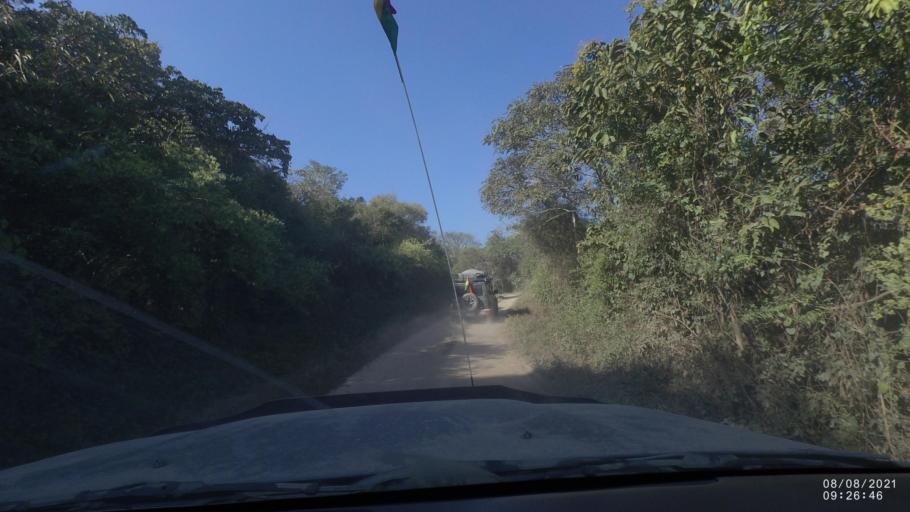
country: BO
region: La Paz
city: Quime
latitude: -16.5891
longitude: -66.7215
